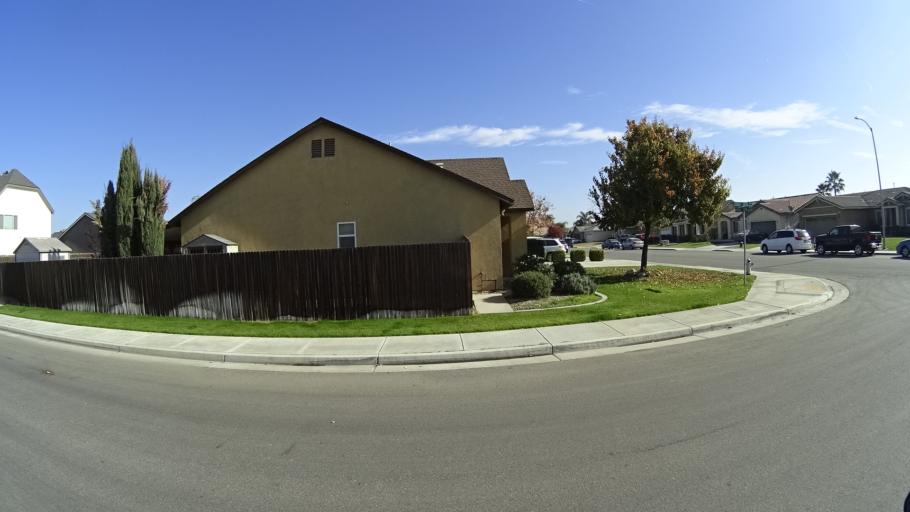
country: US
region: California
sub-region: Kern County
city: Greenfield
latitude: 35.2846
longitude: -119.0634
